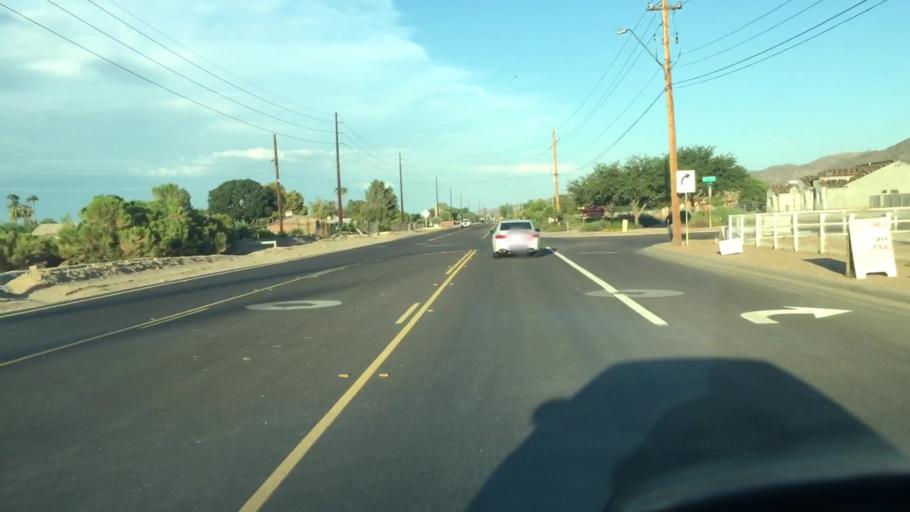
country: US
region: Arizona
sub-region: Maricopa County
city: Laveen
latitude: 33.3632
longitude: -112.1611
